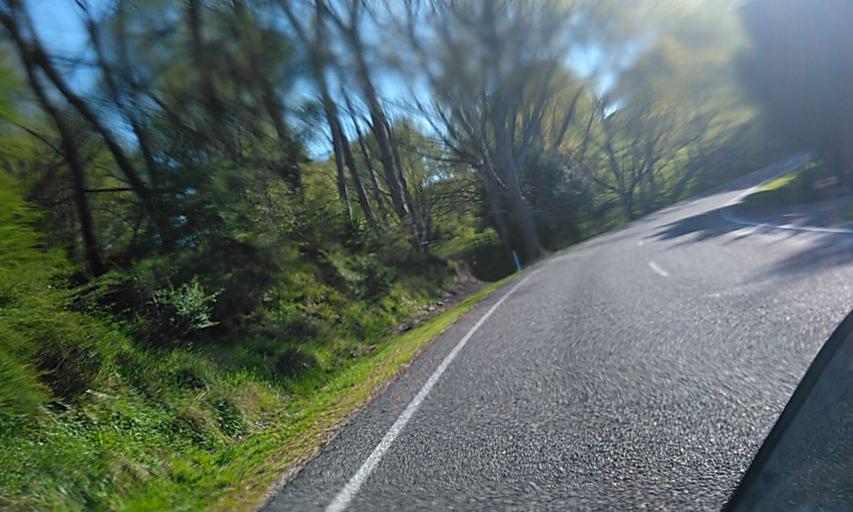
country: NZ
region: Gisborne
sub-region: Gisborne District
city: Gisborne
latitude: -38.5916
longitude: 177.9720
